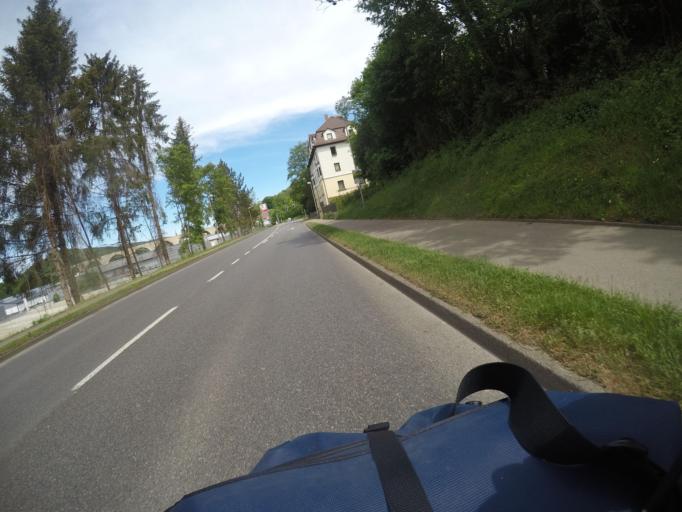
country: DE
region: Baden-Wuerttemberg
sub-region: Karlsruhe Region
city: Nagold
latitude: 48.5426
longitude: 8.7306
